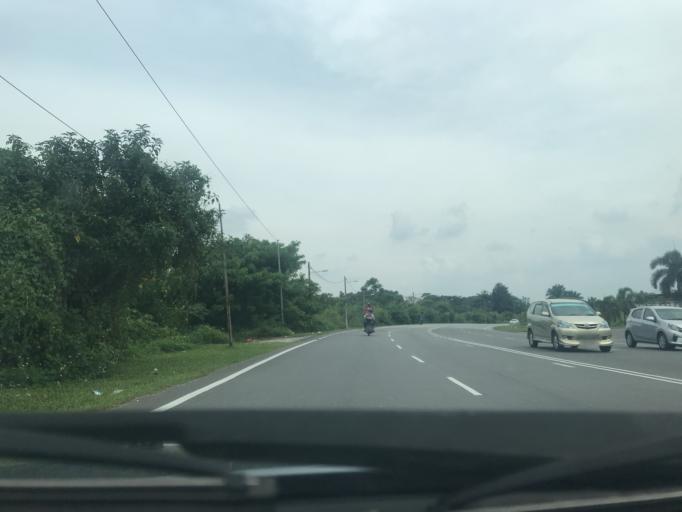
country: MY
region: Perak
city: Ipoh
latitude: 4.6609
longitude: 101.1526
